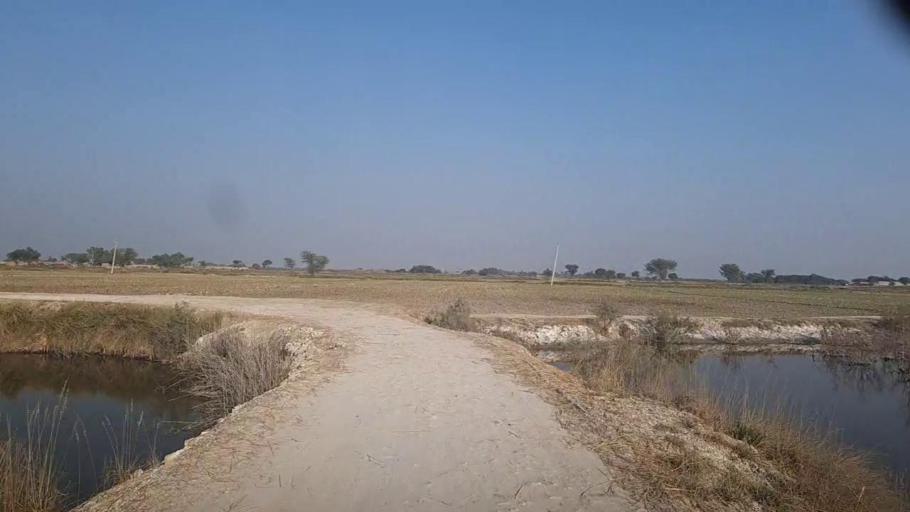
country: PK
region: Sindh
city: Thul
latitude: 28.1615
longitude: 68.8137
